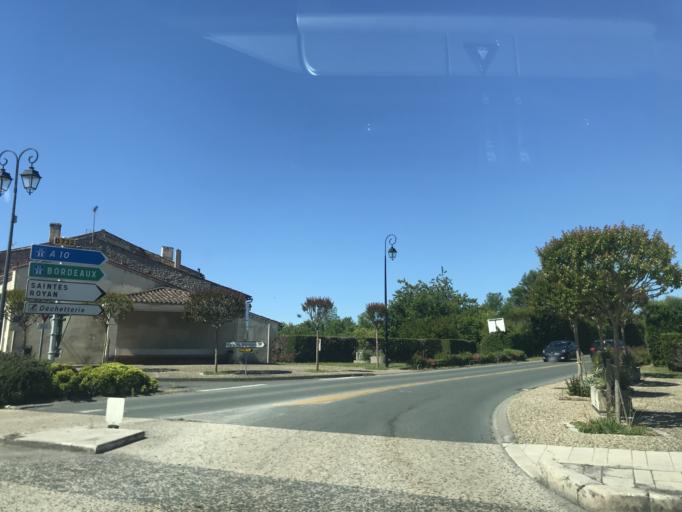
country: FR
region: Poitou-Charentes
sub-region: Departement de la Charente-Maritime
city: Pons
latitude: 45.5727
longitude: -0.5490
